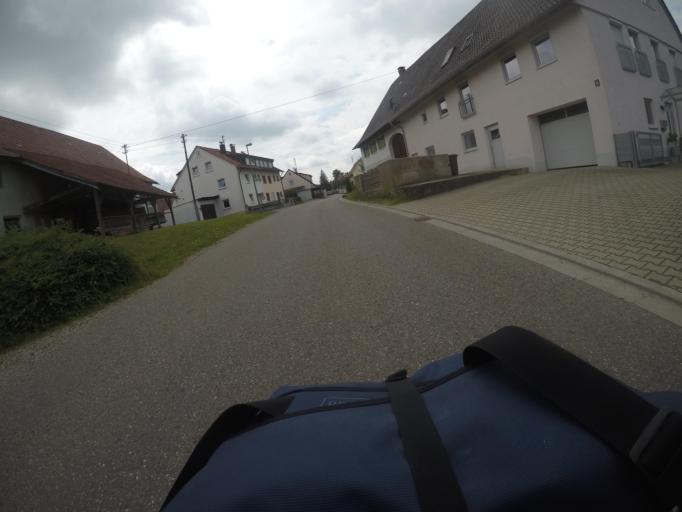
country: DE
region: Bavaria
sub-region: Swabia
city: Heimertingen
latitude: 48.0147
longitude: 10.1657
